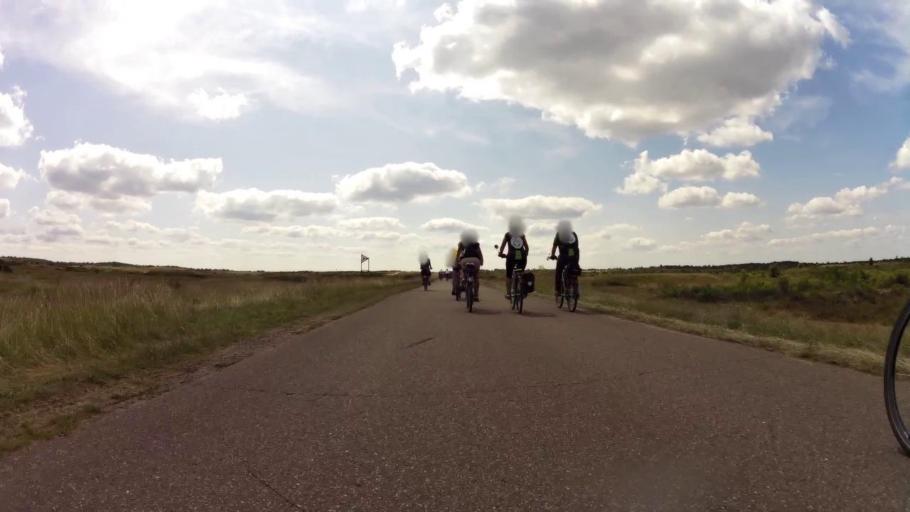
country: PL
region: West Pomeranian Voivodeship
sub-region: Powiat drawski
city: Drawsko Pomorskie
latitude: 53.4252
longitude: 15.7615
